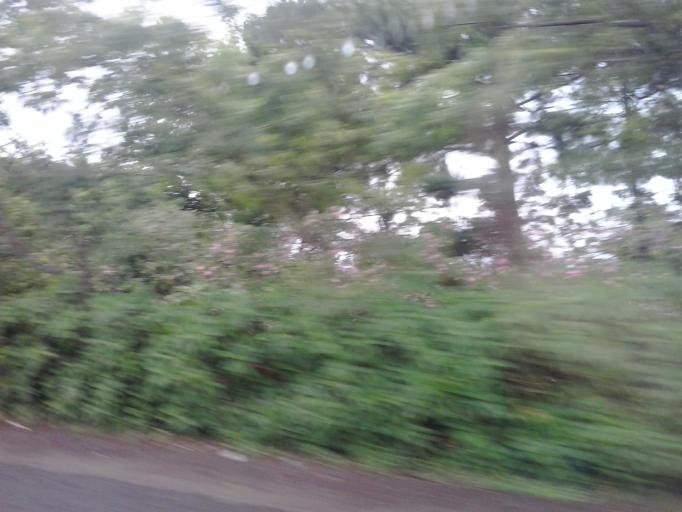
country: BR
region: Rio Grande do Sul
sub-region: Candelaria
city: Candelaria
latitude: -29.7327
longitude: -53.1829
